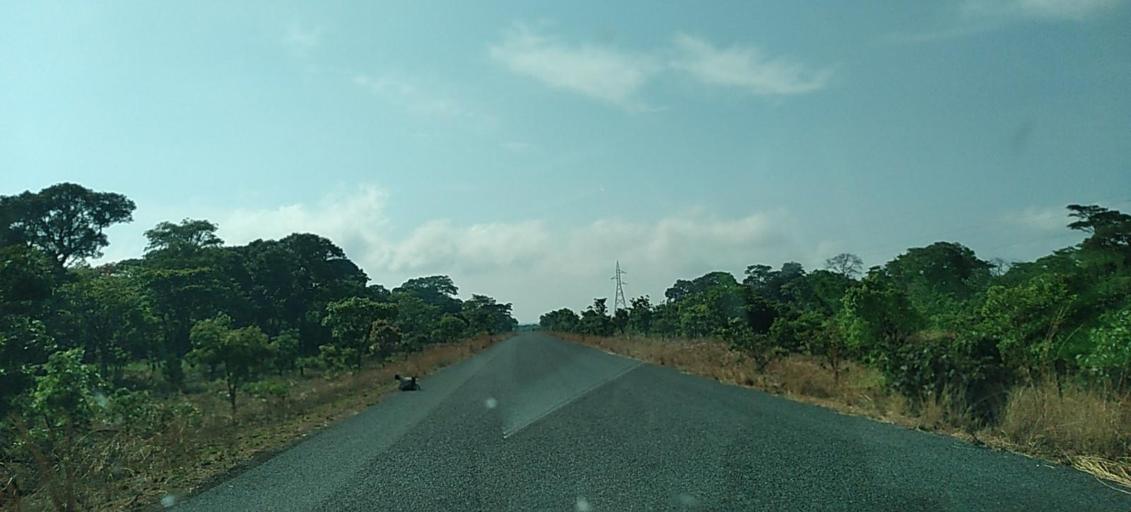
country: ZM
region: North-Western
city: Mwinilunga
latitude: -11.7387
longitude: 24.9827
